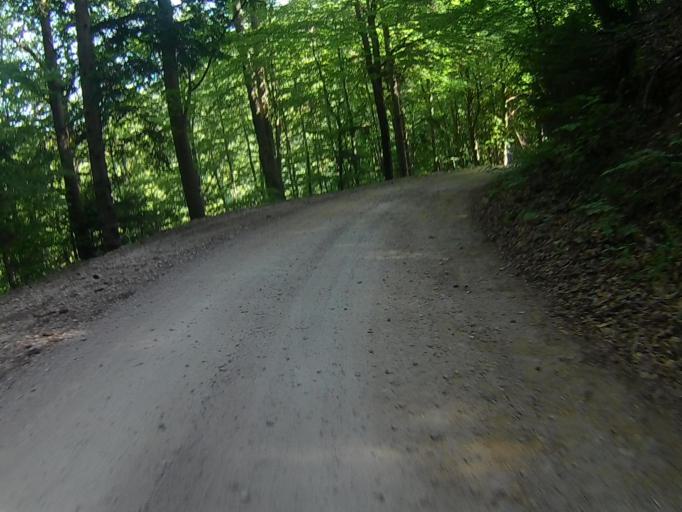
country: SI
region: Maribor
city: Limbus
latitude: 46.5232
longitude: 15.5739
